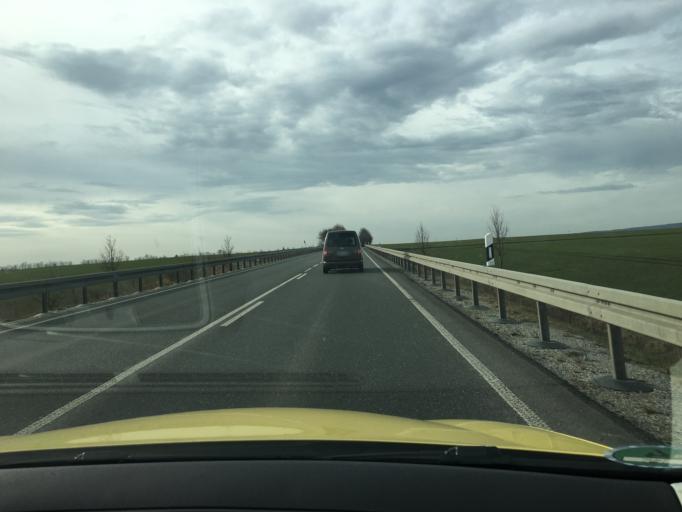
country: DE
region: Thuringia
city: Buttelstedt
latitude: 51.1062
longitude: 11.3503
